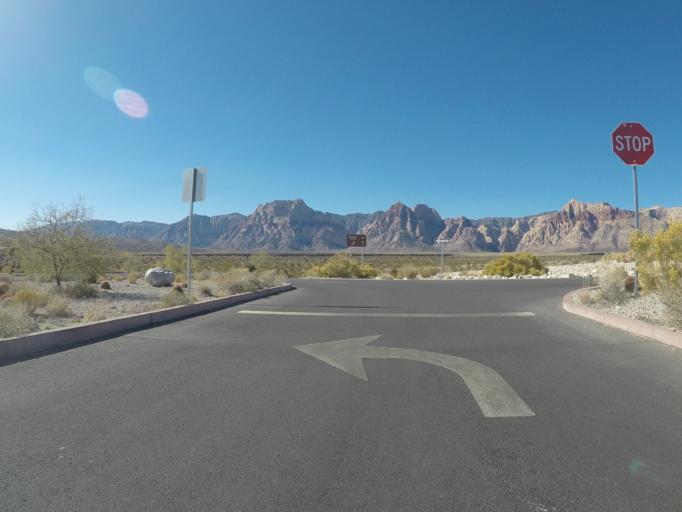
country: US
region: Nevada
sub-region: Clark County
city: Summerlin South
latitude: 36.1349
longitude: -115.4274
